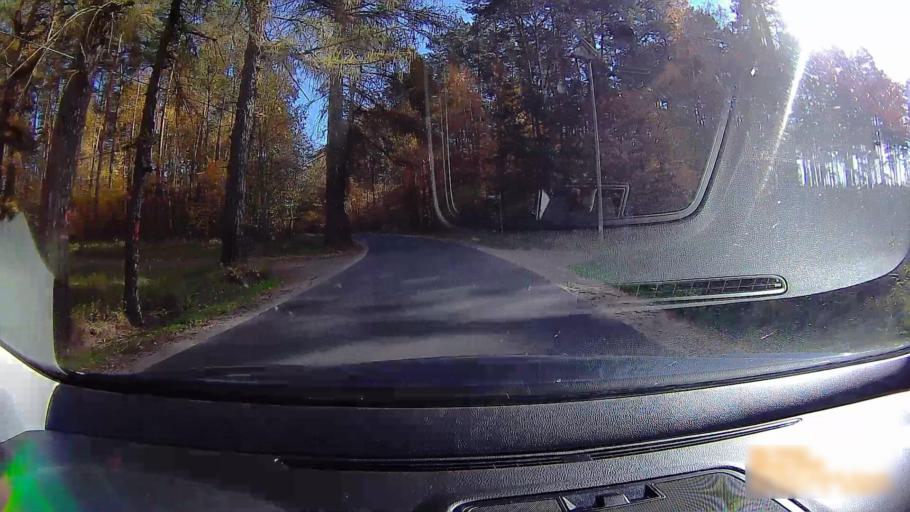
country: PL
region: Greater Poland Voivodeship
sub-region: Powiat ostrzeszowski
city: Ostrzeszow
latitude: 51.4065
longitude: 18.0039
